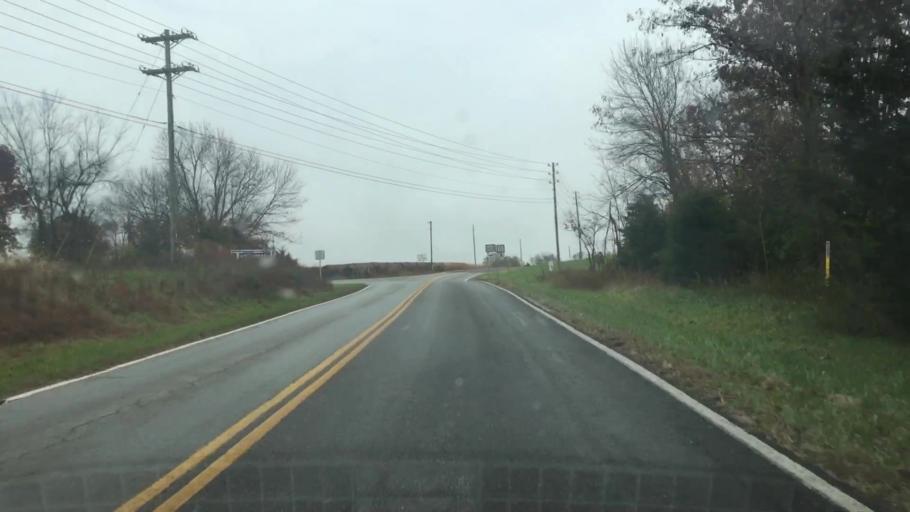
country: US
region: Missouri
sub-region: Callaway County
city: Fulton
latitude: 38.8409
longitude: -91.9246
